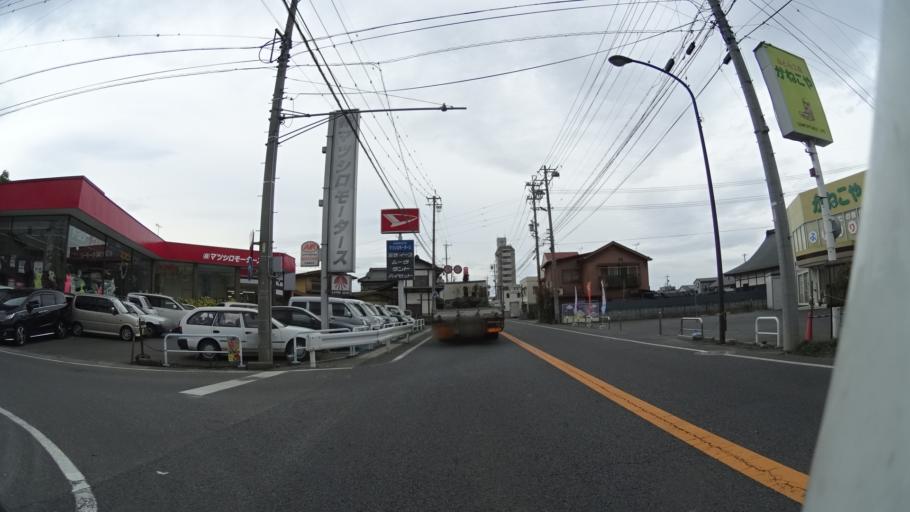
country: JP
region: Nagano
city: Nagano-shi
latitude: 36.5801
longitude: 138.1475
